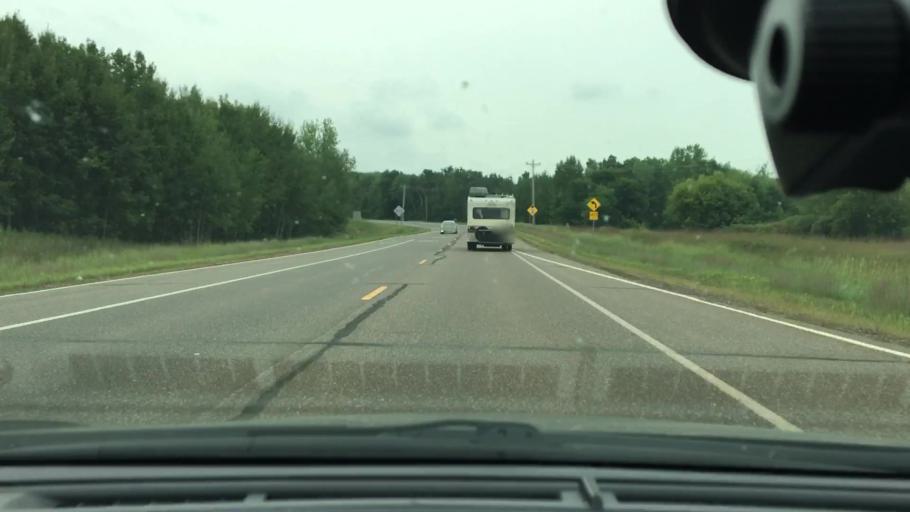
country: US
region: Minnesota
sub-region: Crow Wing County
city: Crosby
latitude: 46.4909
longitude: -93.9566
